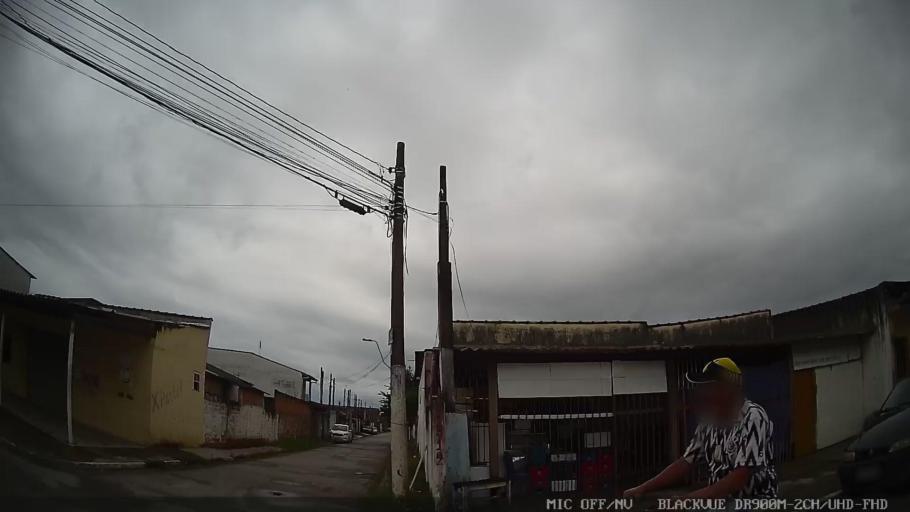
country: BR
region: Sao Paulo
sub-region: Sao Sebastiao
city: Sao Sebastiao
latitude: -23.7105
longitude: -45.4427
